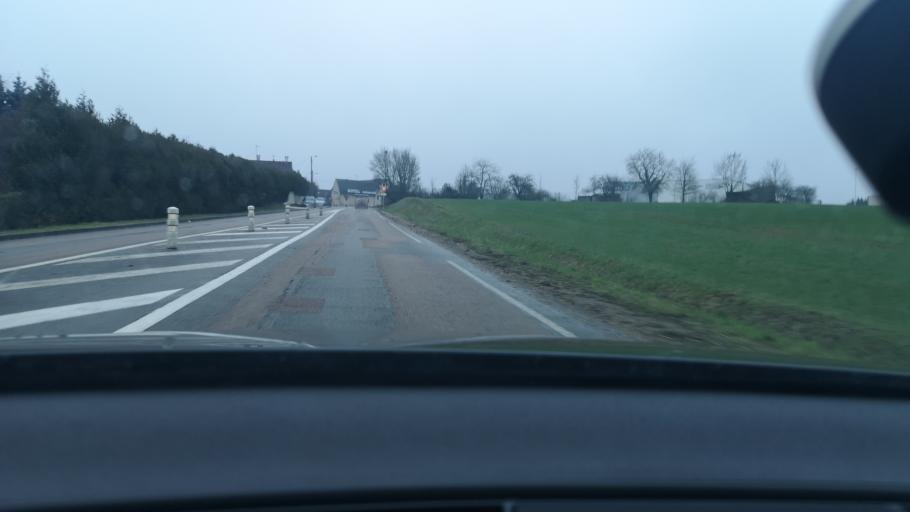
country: FR
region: Bourgogne
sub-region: Departement de la Cote-d'Or
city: Fenay
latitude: 47.2456
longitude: 5.0568
